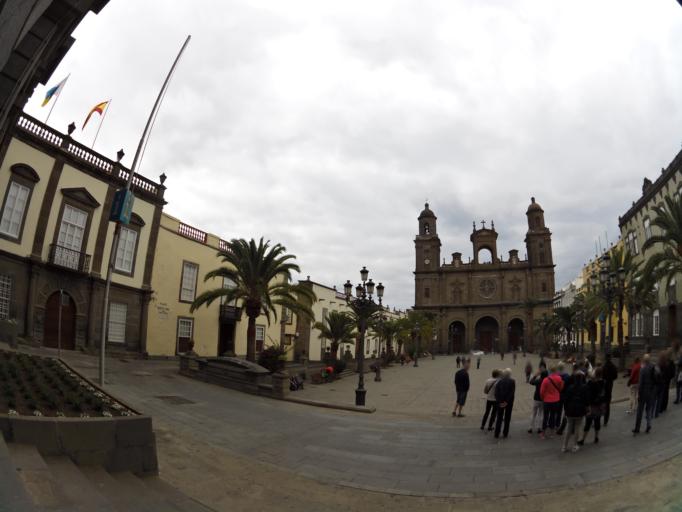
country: ES
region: Canary Islands
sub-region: Provincia de Las Palmas
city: Las Palmas de Gran Canaria
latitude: 28.1003
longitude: -15.4161
